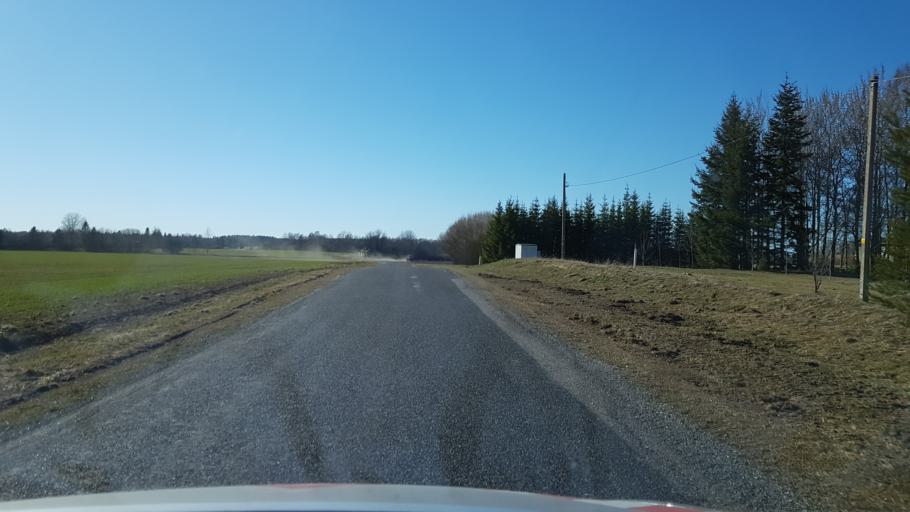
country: EE
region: Laeaene-Virumaa
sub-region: Kadrina vald
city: Kadrina
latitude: 59.4428
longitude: 26.1175
